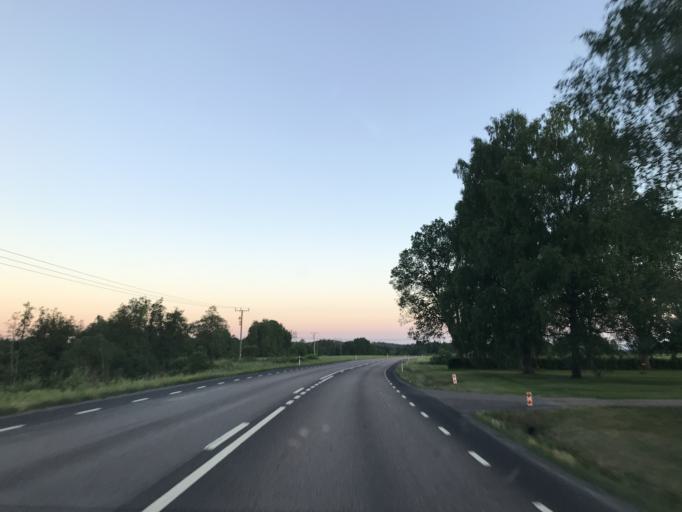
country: SE
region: Vaestra Goetaland
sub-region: Marks Kommun
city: Horred
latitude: 57.3868
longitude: 12.5211
